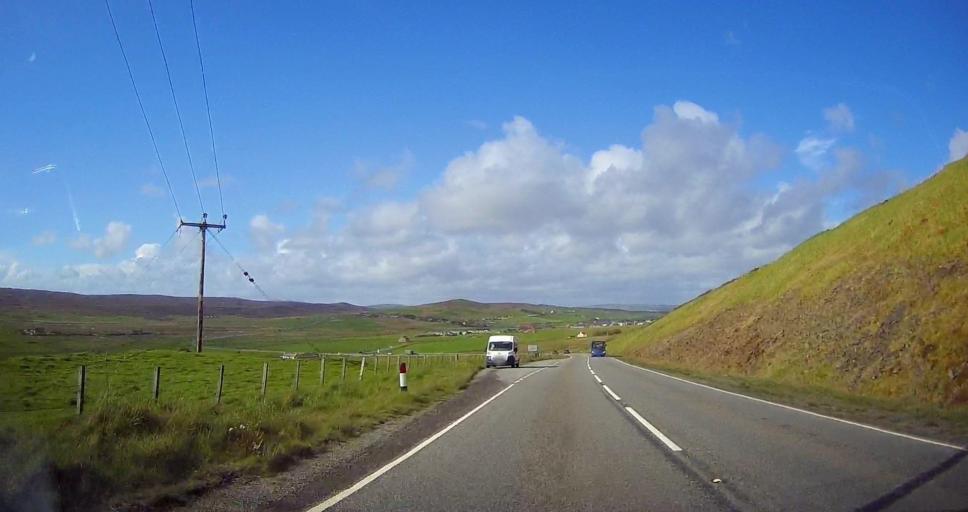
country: GB
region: Scotland
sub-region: Shetland Islands
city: Lerwick
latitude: 60.1813
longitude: -1.2252
